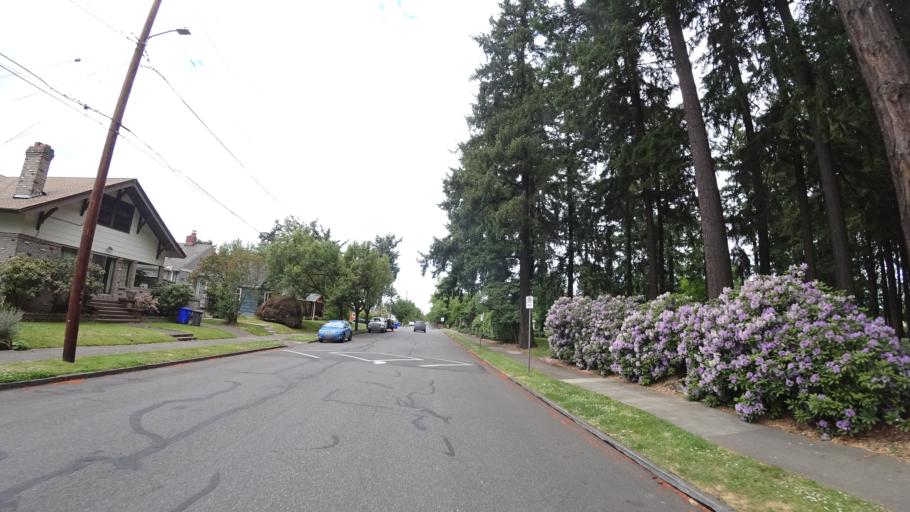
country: US
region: Oregon
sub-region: Multnomah County
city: Portland
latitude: 45.5800
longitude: -122.7135
